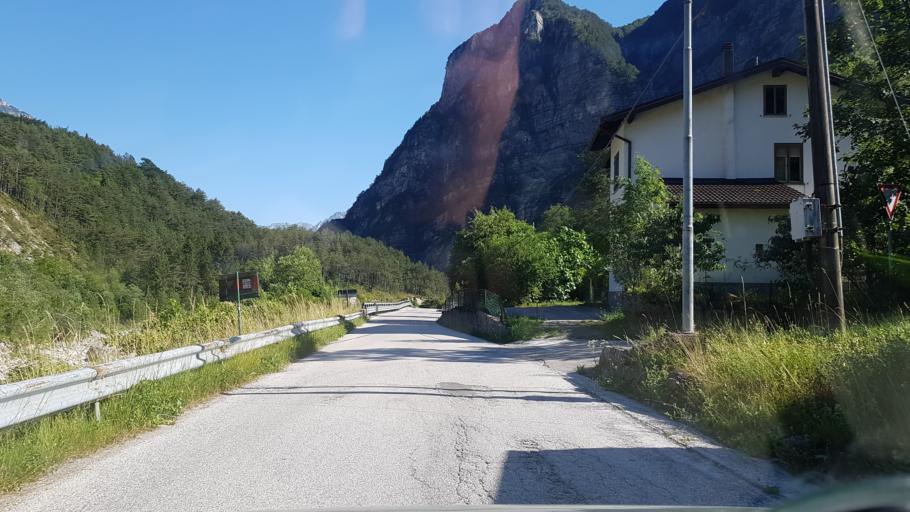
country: IT
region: Friuli Venezia Giulia
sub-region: Provincia di Udine
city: Moggio Udinese
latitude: 46.4509
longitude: 13.1874
